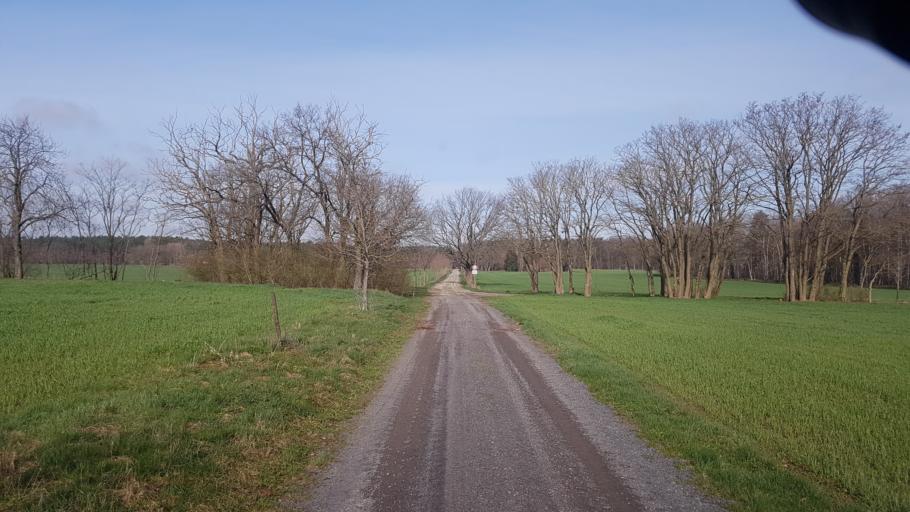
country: DE
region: Brandenburg
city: Hohenbucko
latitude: 51.6880
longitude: 13.4687
